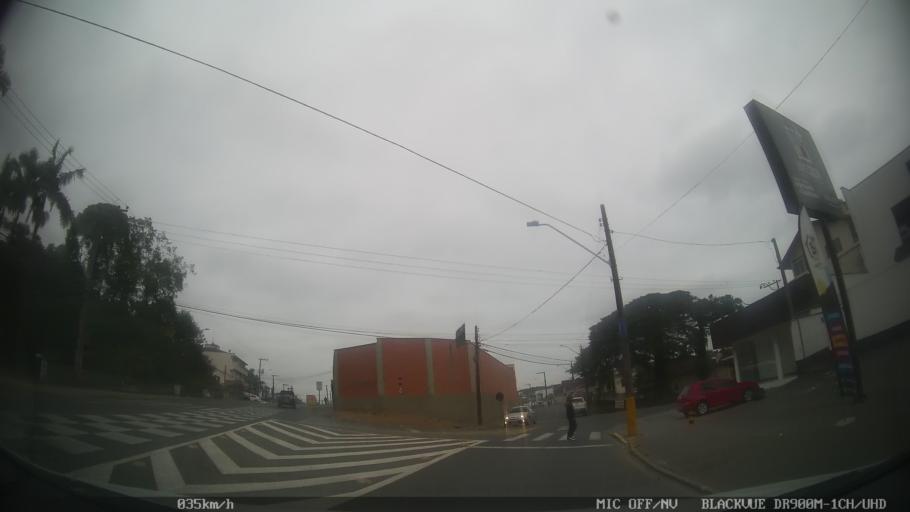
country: BR
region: Santa Catarina
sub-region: Joinville
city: Joinville
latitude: -26.3428
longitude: -48.8474
